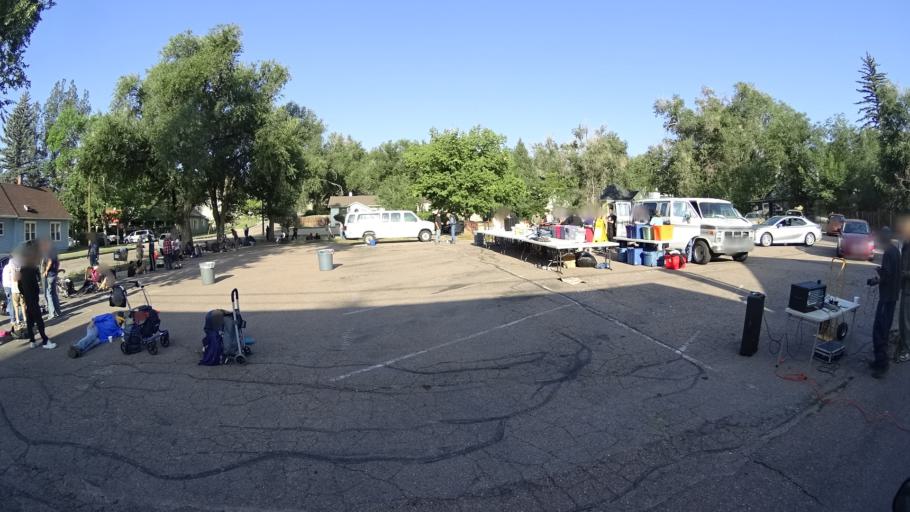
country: US
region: Colorado
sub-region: El Paso County
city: Colorado Springs
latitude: 38.8409
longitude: -104.8342
